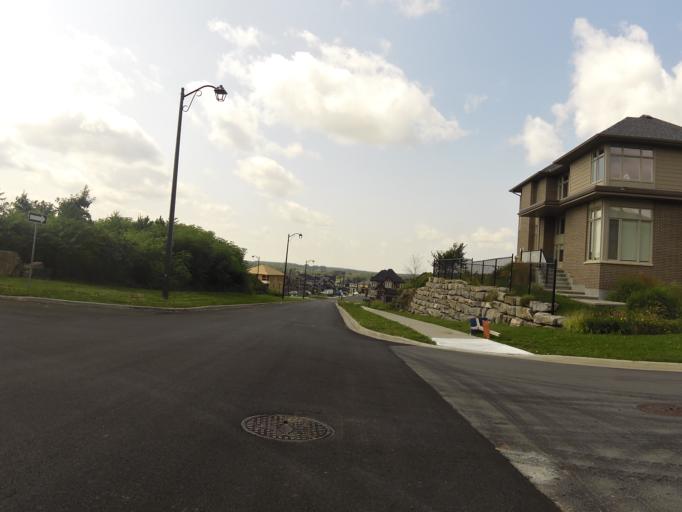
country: CA
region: Ontario
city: Bells Corners
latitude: 45.3186
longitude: -75.9386
